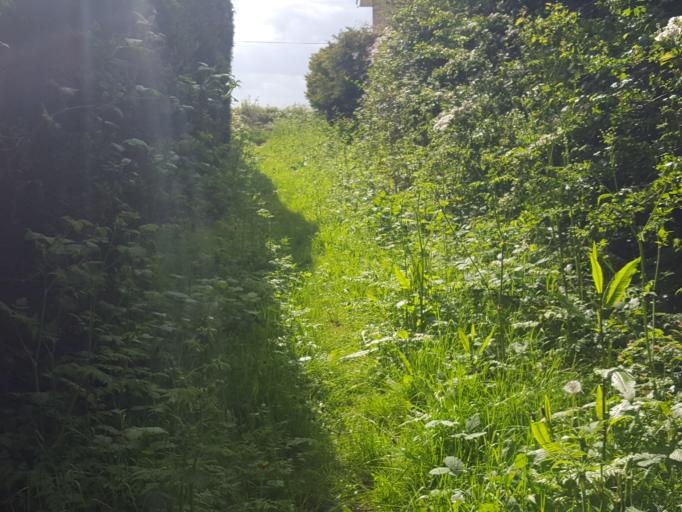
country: GB
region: England
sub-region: Essex
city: Frinton-on-Sea
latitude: 51.8343
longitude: 1.2076
